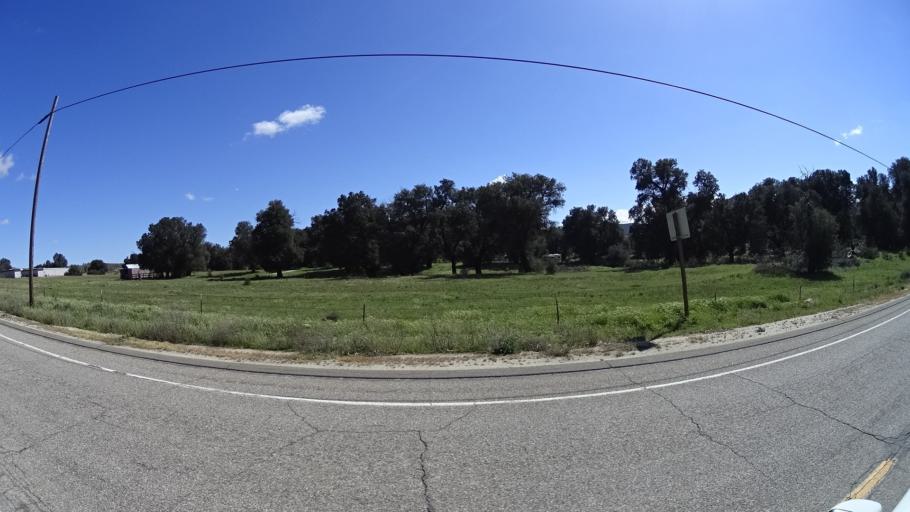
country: US
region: California
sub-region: San Diego County
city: Julian
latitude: 33.2103
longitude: -116.5353
